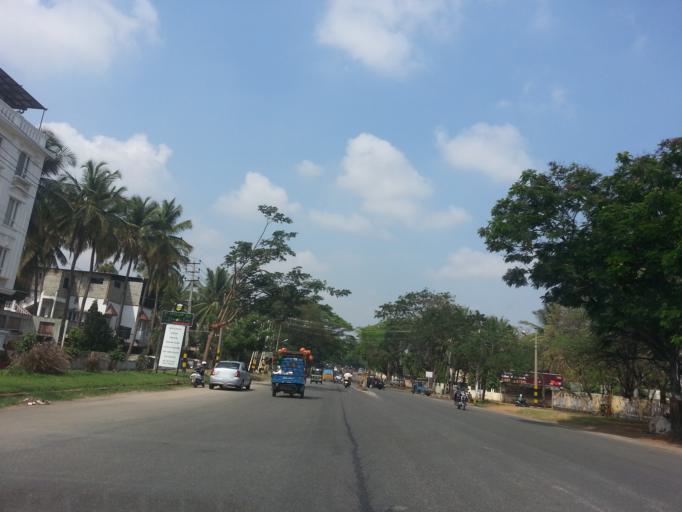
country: IN
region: Karnataka
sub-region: Mysore
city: Mysore
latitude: 12.3323
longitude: 76.6519
